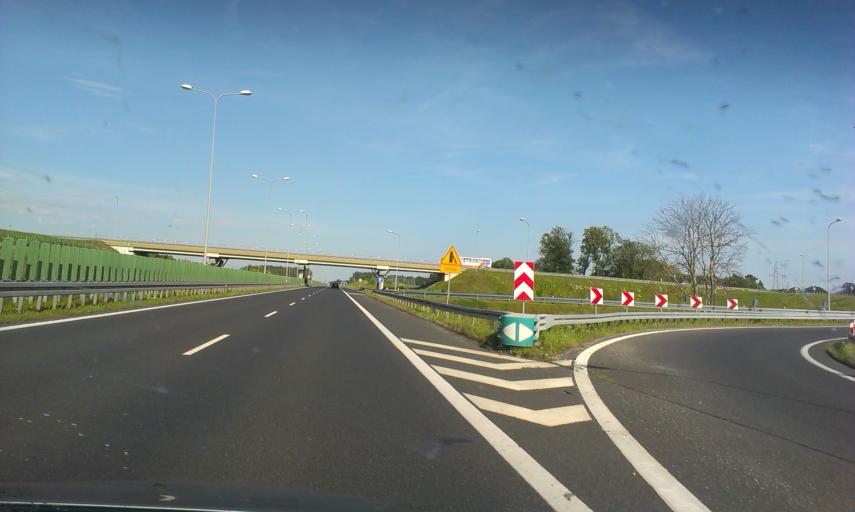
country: PL
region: Greater Poland Voivodeship
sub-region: Powiat pilski
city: Wyrzysk
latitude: 53.1629
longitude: 17.2213
